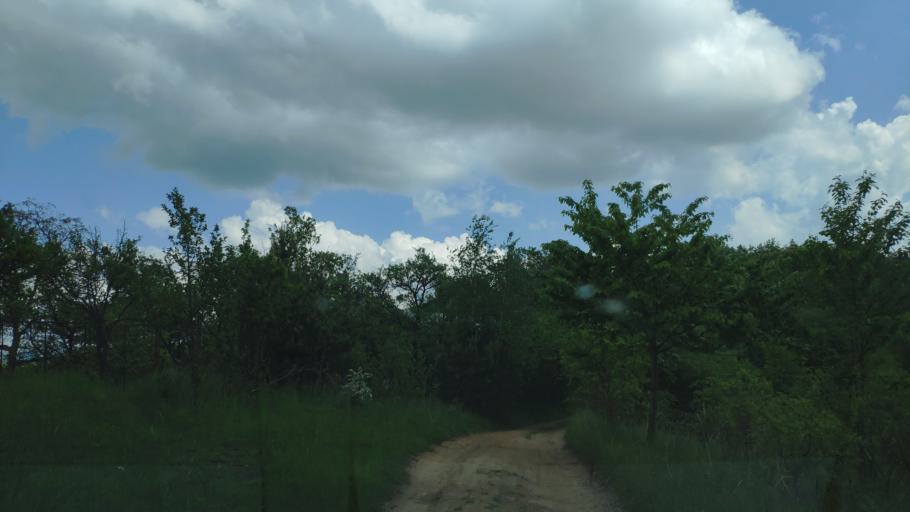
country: SK
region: Presovsky
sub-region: Okres Presov
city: Presov
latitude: 48.9392
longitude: 21.1202
